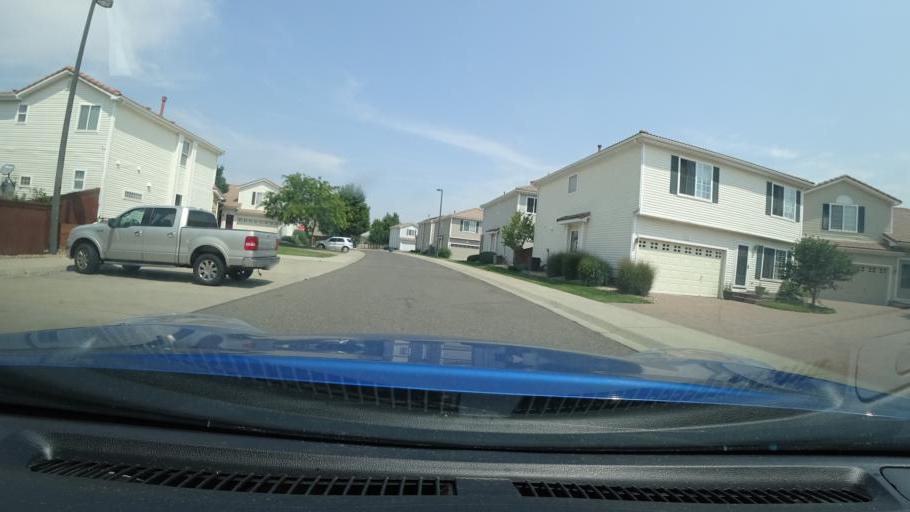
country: US
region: Colorado
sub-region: Adams County
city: Aurora
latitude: 39.7756
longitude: -104.7541
